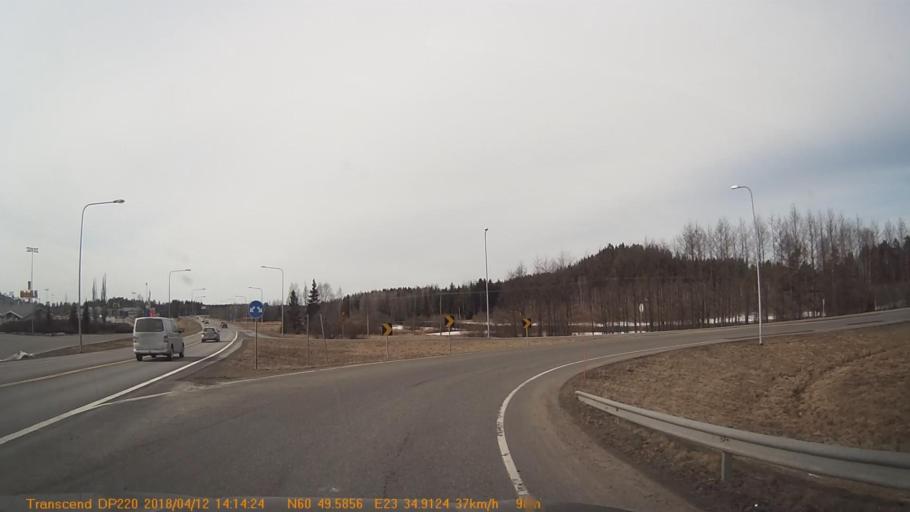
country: FI
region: Haeme
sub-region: Forssa
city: Forssa
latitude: 60.8265
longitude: 23.5817
